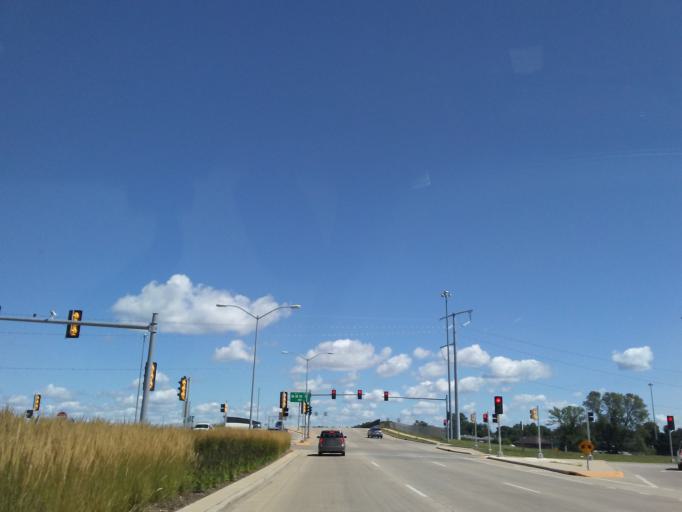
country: US
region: Wisconsin
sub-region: Dane County
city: Madison
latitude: 43.0329
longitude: -89.4079
